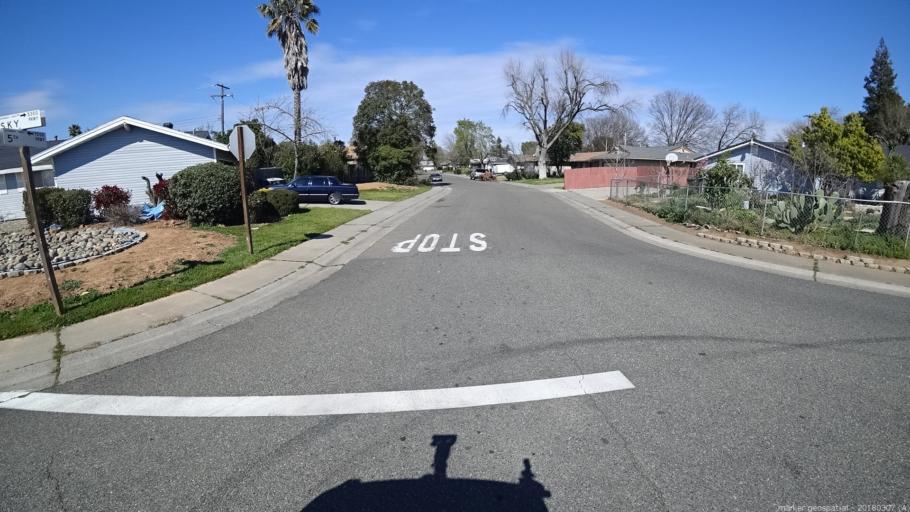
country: US
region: California
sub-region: Sacramento County
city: Parkway
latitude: 38.4997
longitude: -121.4438
